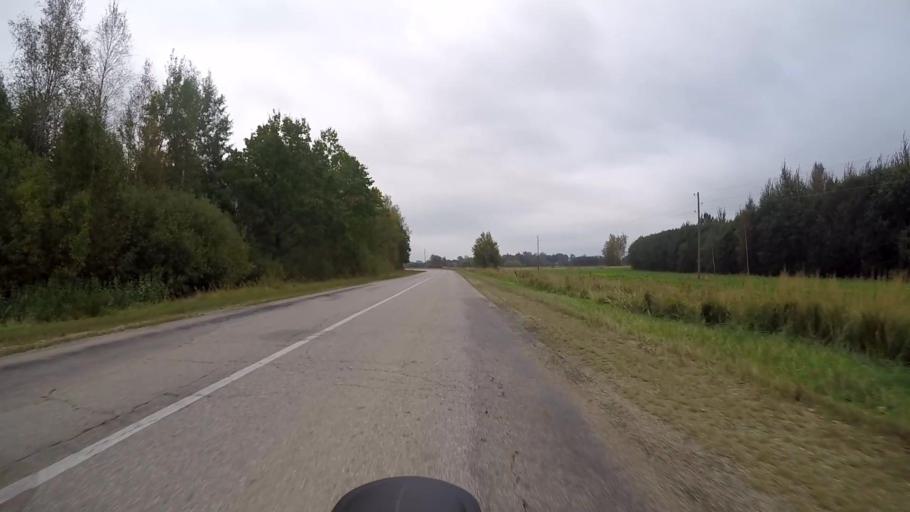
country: LV
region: Saulkrastu
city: Saulkrasti
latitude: 57.2750
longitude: 24.5507
